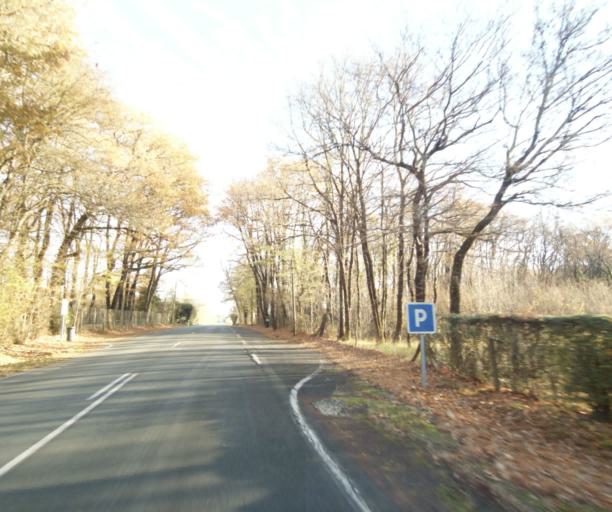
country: FR
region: Poitou-Charentes
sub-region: Departement de la Charente-Maritime
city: Saint-Georges-des-Coteaux
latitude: 45.7346
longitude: -0.7083
